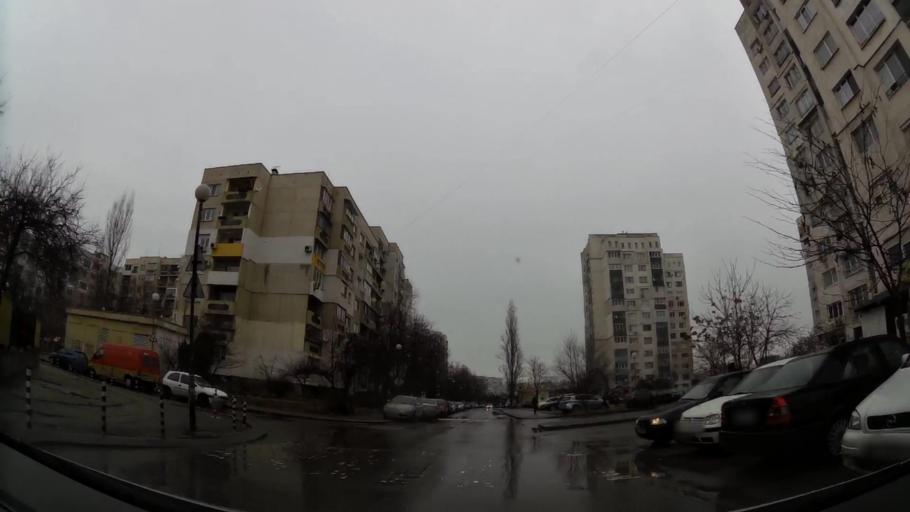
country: BG
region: Sofia-Capital
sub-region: Stolichna Obshtina
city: Sofia
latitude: 42.6527
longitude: 23.4005
